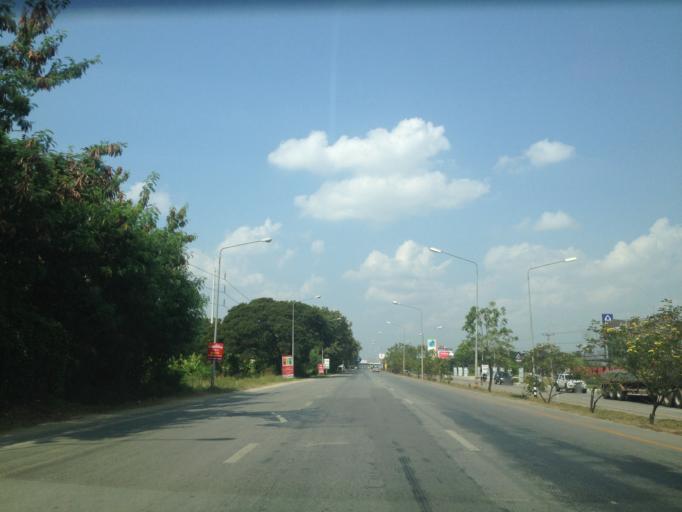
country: TH
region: Chiang Mai
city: Saraphi
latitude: 18.7436
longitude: 99.0349
